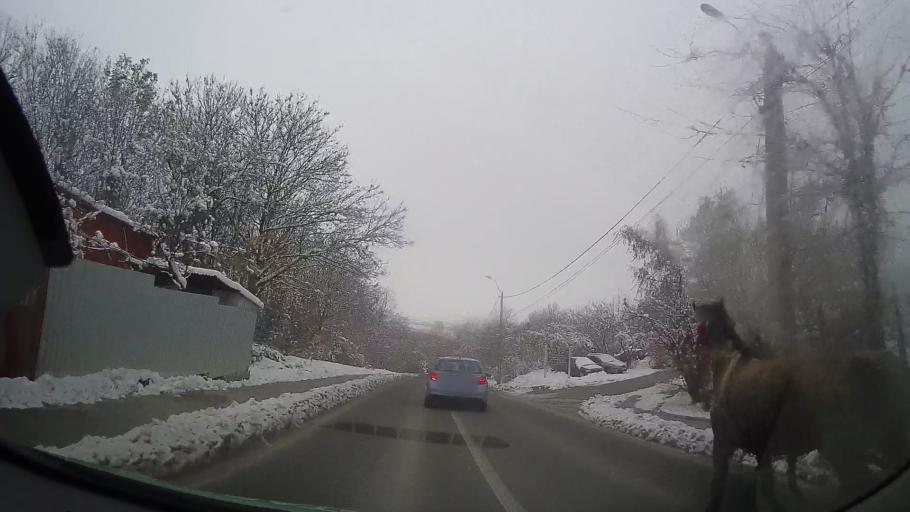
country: RO
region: Vaslui
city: Vaslui
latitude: 46.6476
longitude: 27.7221
